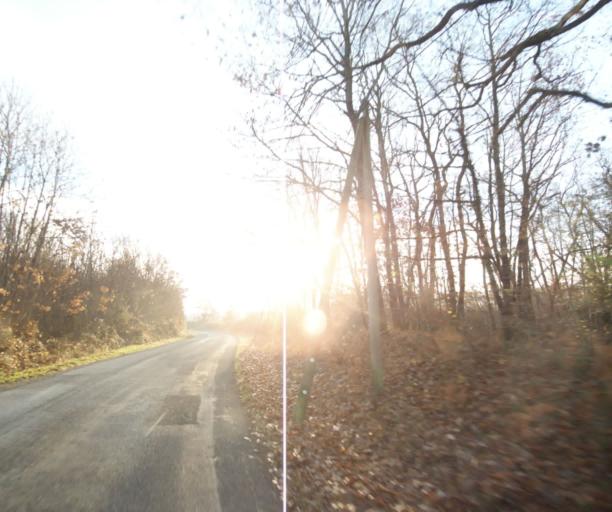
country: FR
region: Poitou-Charentes
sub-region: Departement de la Charente-Maritime
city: Fontcouverte
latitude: 45.7705
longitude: -0.5726
